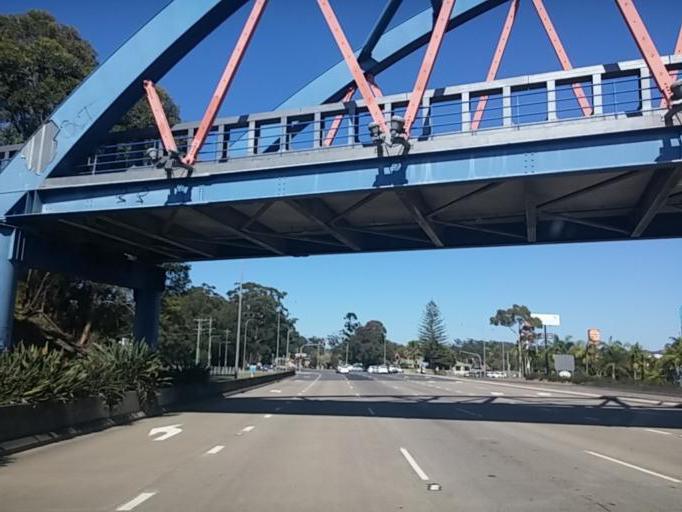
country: AU
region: New South Wales
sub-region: Coffs Harbour
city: Coffs Harbour
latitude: -30.2829
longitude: 153.1280
